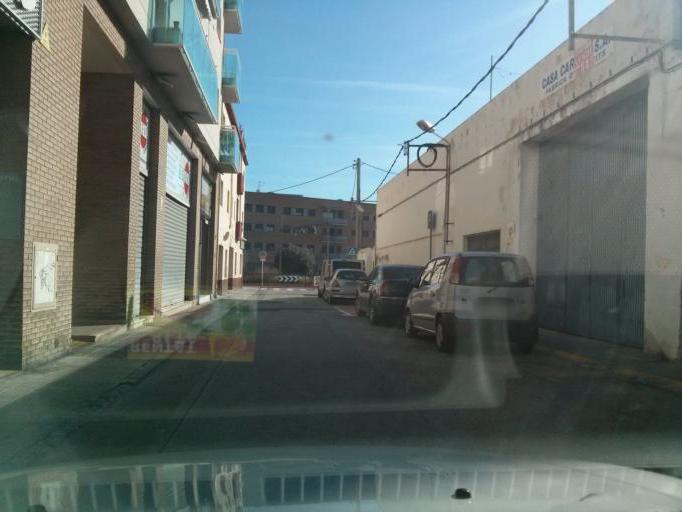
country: ES
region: Catalonia
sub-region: Provincia de Tarragona
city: El Vendrell
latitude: 41.2228
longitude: 1.5388
